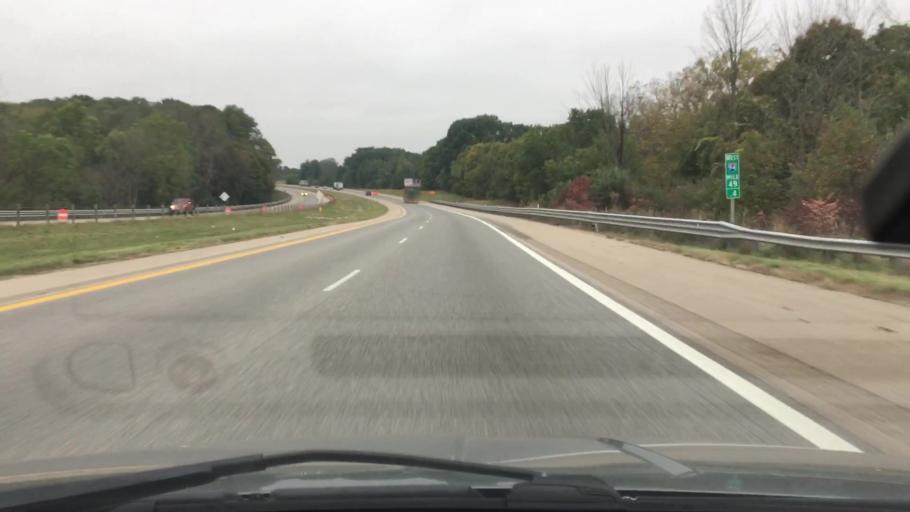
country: US
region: Michigan
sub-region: Van Buren County
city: Hartford
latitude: 42.1976
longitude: -86.0963
